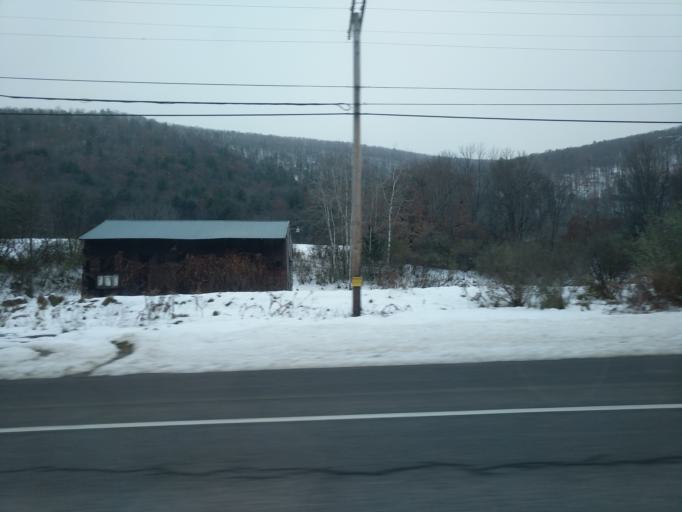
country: US
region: Pennsylvania
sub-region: Tioga County
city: Wellsboro
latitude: 41.8032
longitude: -77.2991
